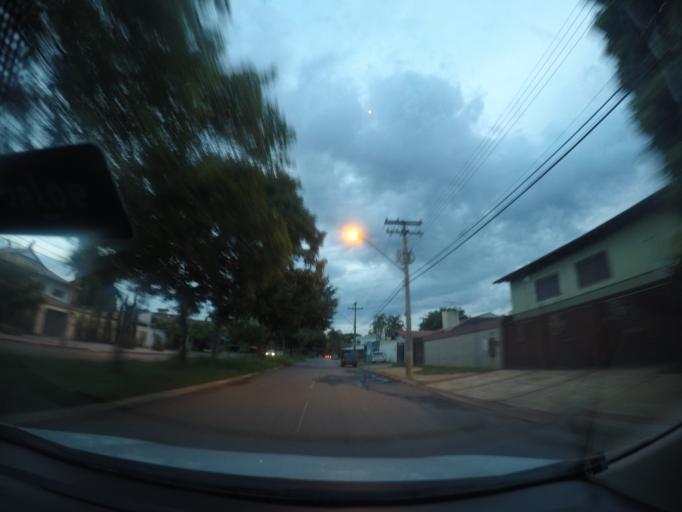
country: BR
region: Goias
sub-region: Goiania
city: Goiania
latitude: -16.6481
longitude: -49.2283
